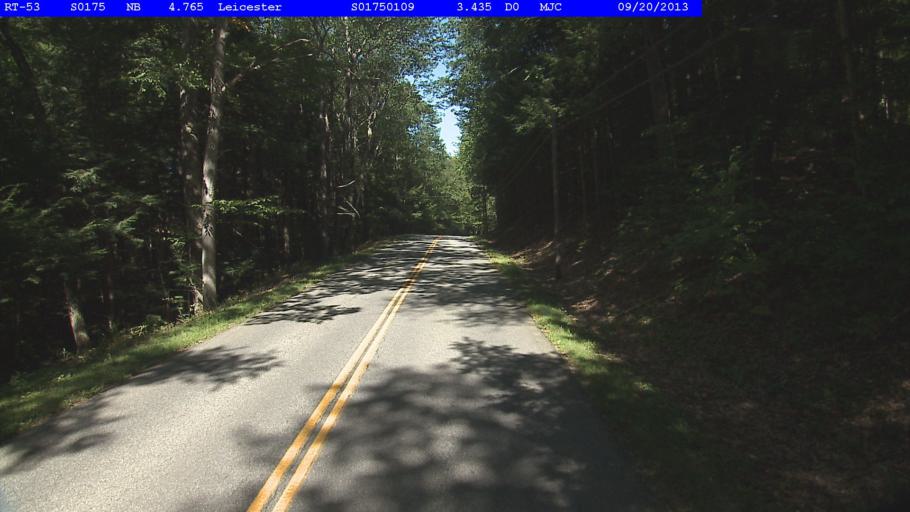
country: US
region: Vermont
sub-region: Rutland County
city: Brandon
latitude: 43.8920
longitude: -73.0650
